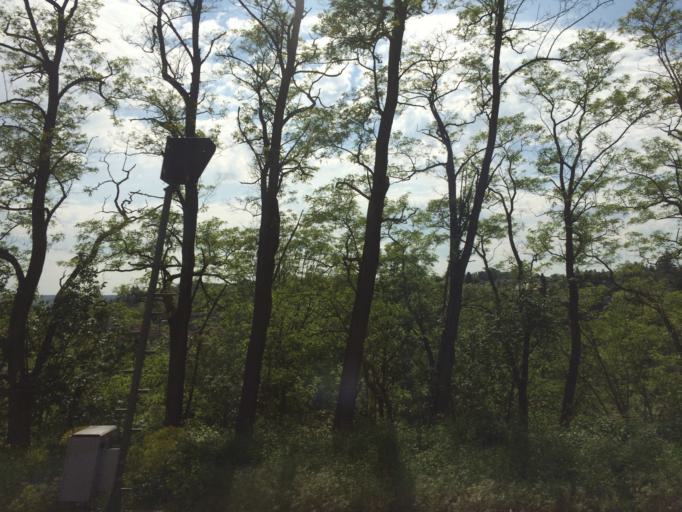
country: DE
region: Bavaria
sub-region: Regierungsbezirk Unterfranken
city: Kitzingen
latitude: 49.7289
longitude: 10.1574
